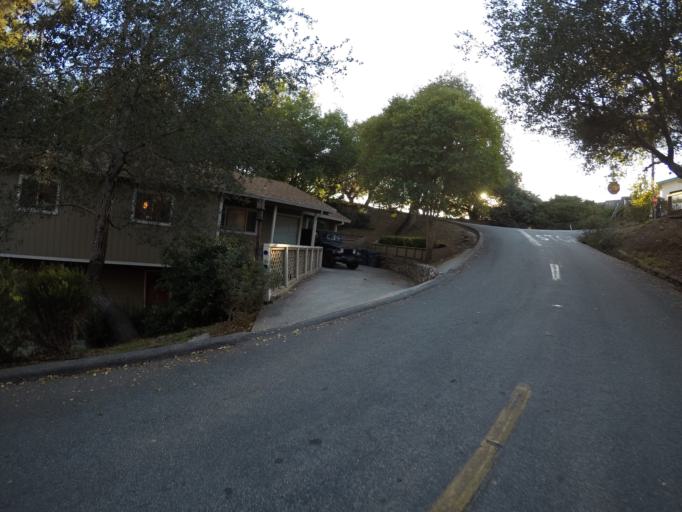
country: US
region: California
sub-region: Santa Cruz County
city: Scotts Valley
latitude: 37.0733
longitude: -121.9971
